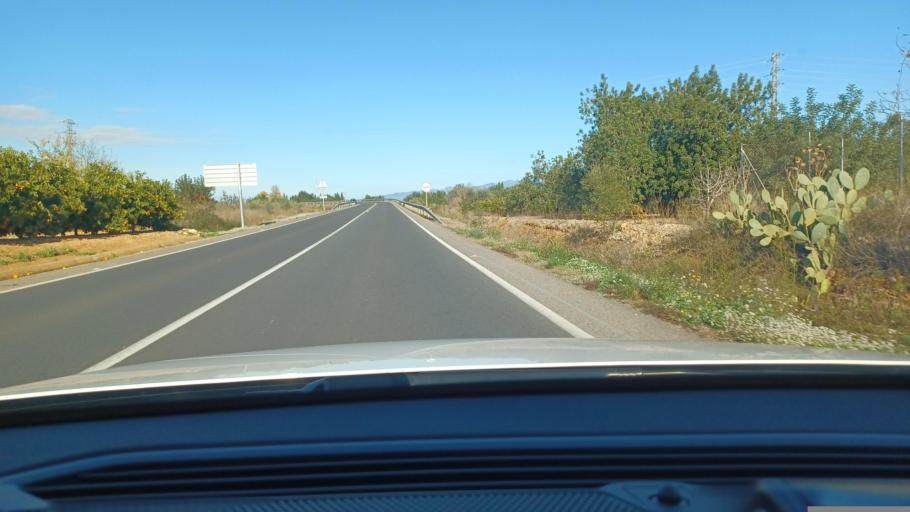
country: ES
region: Catalonia
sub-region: Provincia de Tarragona
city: Santa Barbara
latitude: 40.7177
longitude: 0.5058
